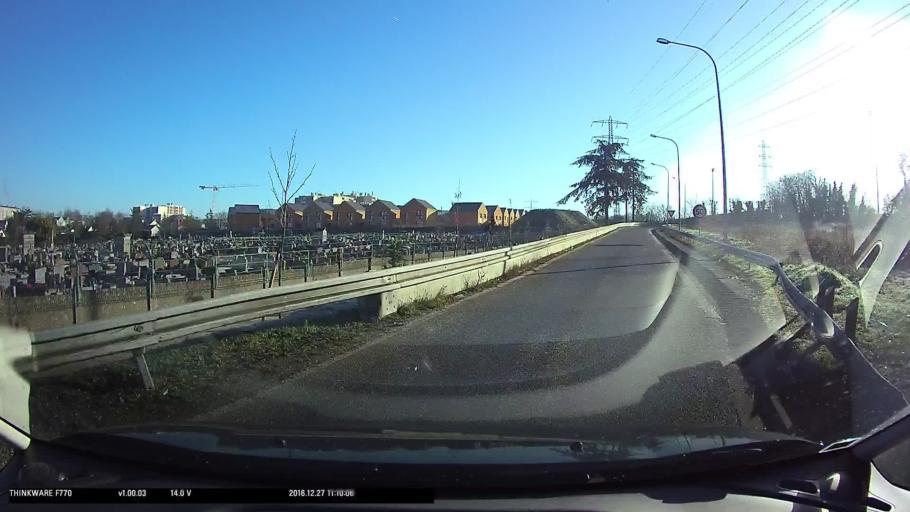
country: FR
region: Ile-de-France
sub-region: Departement du Val-d'Oise
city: Pontoise
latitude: 49.0351
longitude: 2.1027
